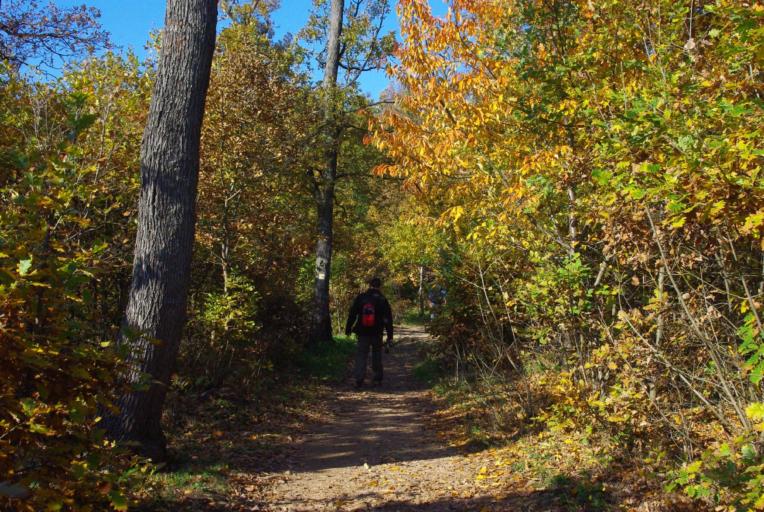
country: HU
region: Pest
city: Budakeszi
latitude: 47.5317
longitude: 18.9612
